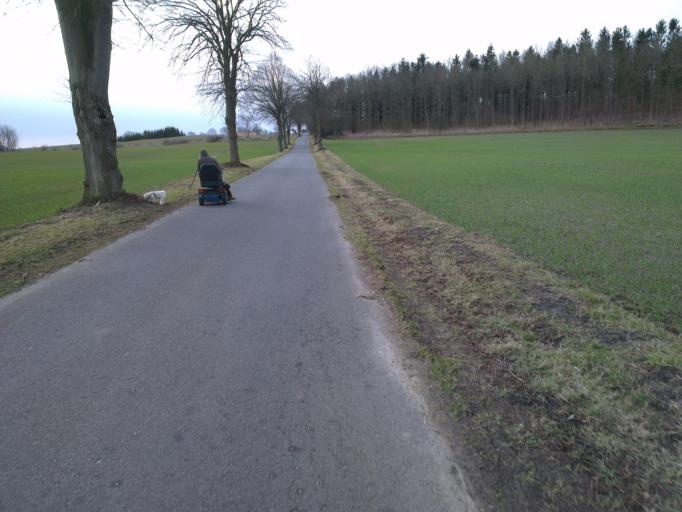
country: DK
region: Capital Region
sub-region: Frederikssund Kommune
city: Skibby
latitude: 55.7924
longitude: 11.9606
